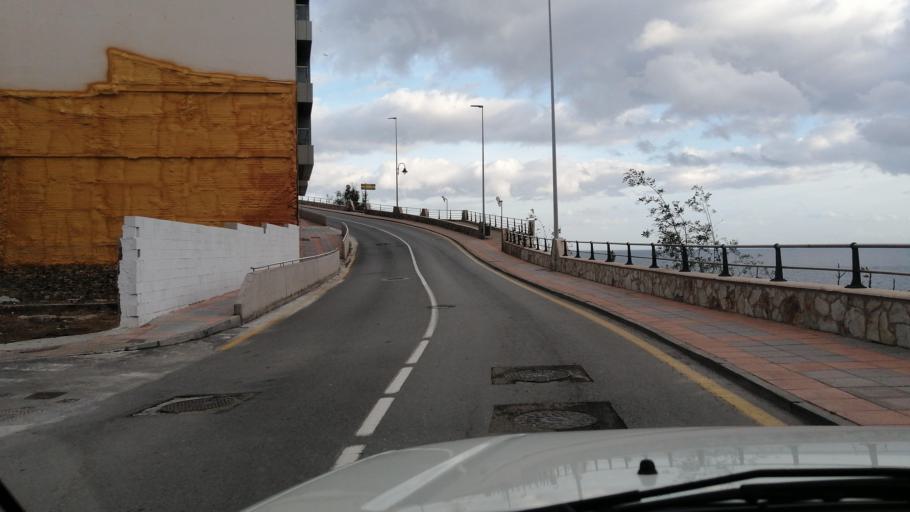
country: ES
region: Ceuta
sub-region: Ceuta
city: Ceuta
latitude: 35.8855
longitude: -5.3106
